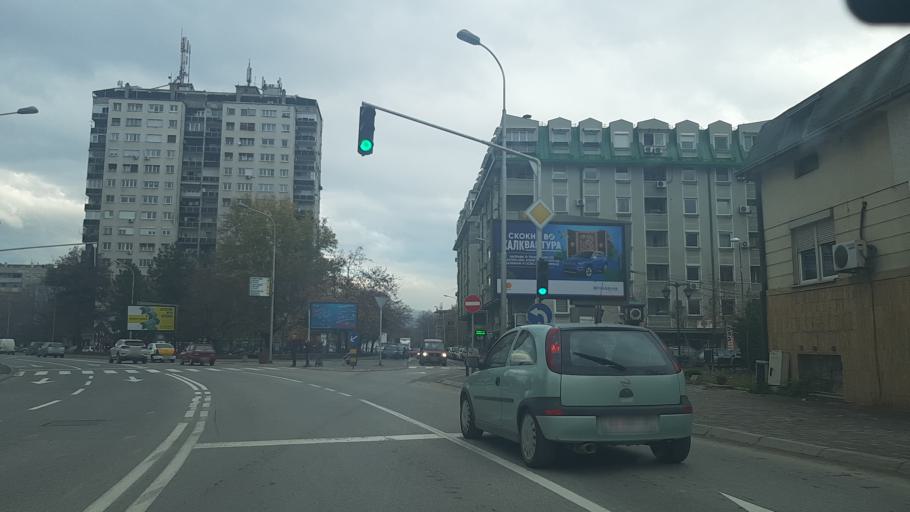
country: MK
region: Karpos
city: Skopje
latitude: 41.9816
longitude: 21.4404
